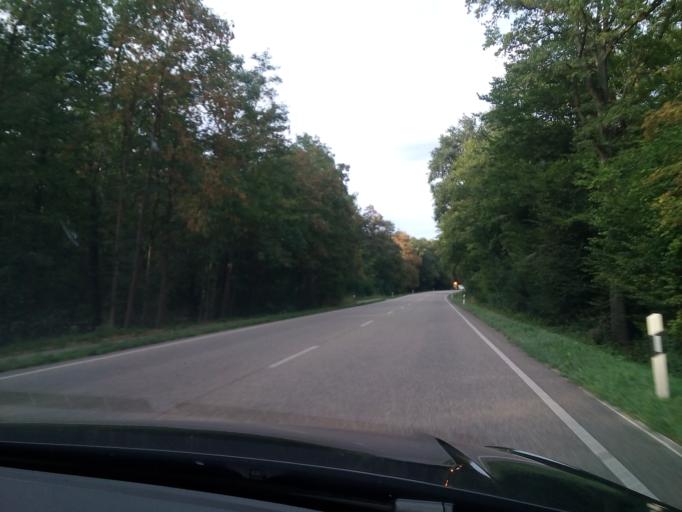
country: DE
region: Baden-Wuerttemberg
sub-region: Freiburg Region
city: Renchen
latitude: 48.5785
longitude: 7.9999
